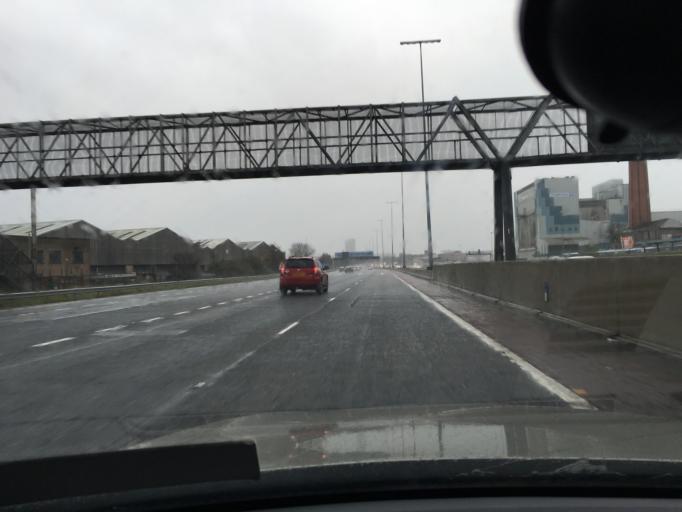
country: GB
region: Northern Ireland
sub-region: City of Belfast
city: Belfast
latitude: 54.6175
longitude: -5.9207
